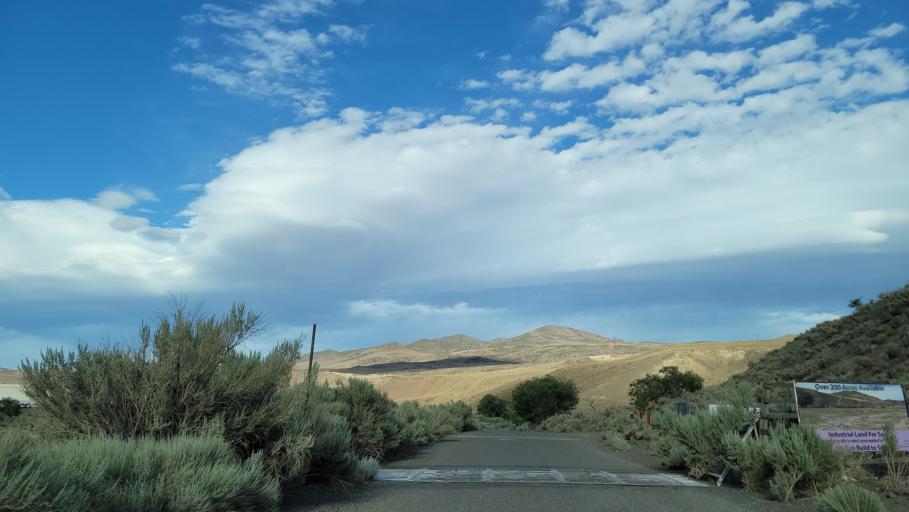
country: US
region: Nevada
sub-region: Washoe County
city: Sparks
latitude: 39.5096
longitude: -119.6328
